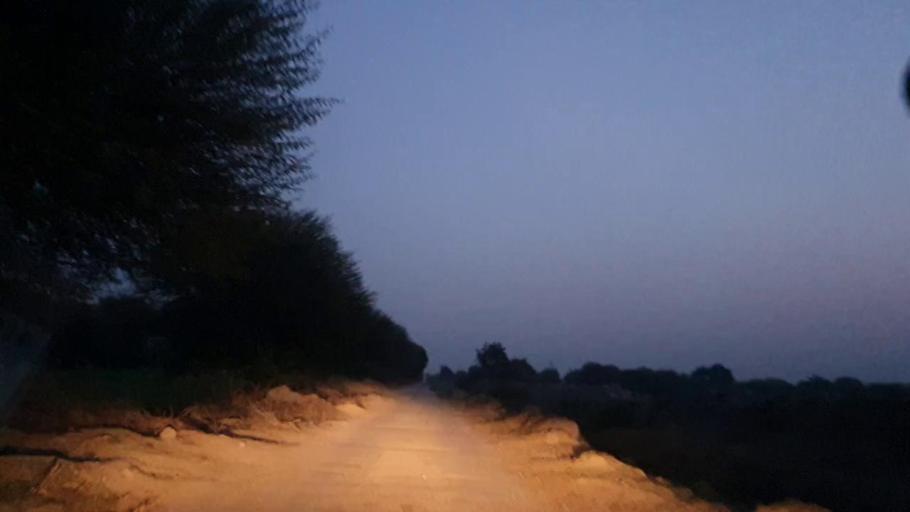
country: PK
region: Sindh
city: Tando Ghulam Ali
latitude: 25.0948
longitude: 68.9152
